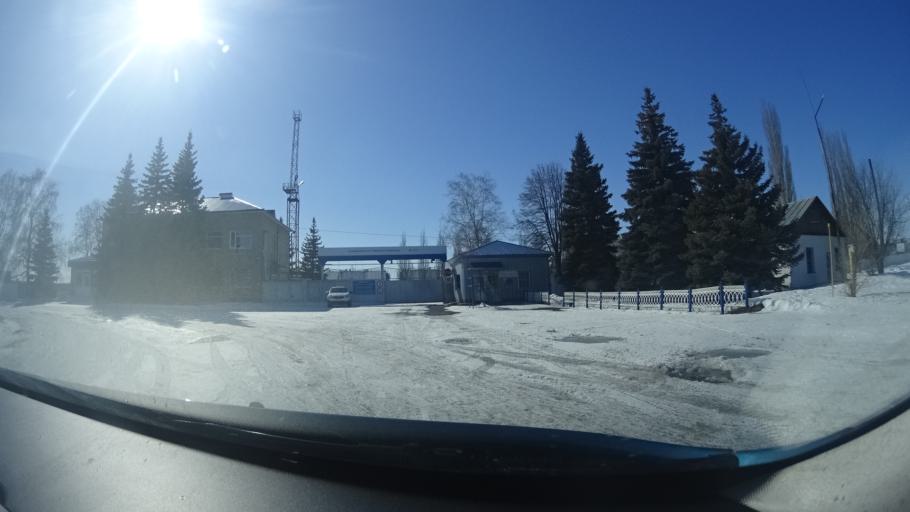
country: RU
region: Bashkortostan
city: Chishmy
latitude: 54.5890
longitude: 55.4079
